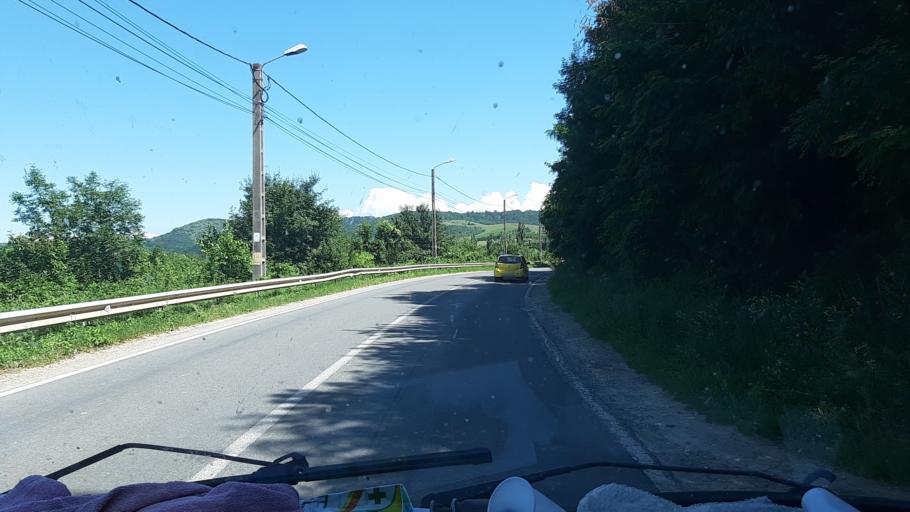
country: RO
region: Caras-Severin
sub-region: Oras Bocsa
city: Bocsa
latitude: 45.3798
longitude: 21.7430
